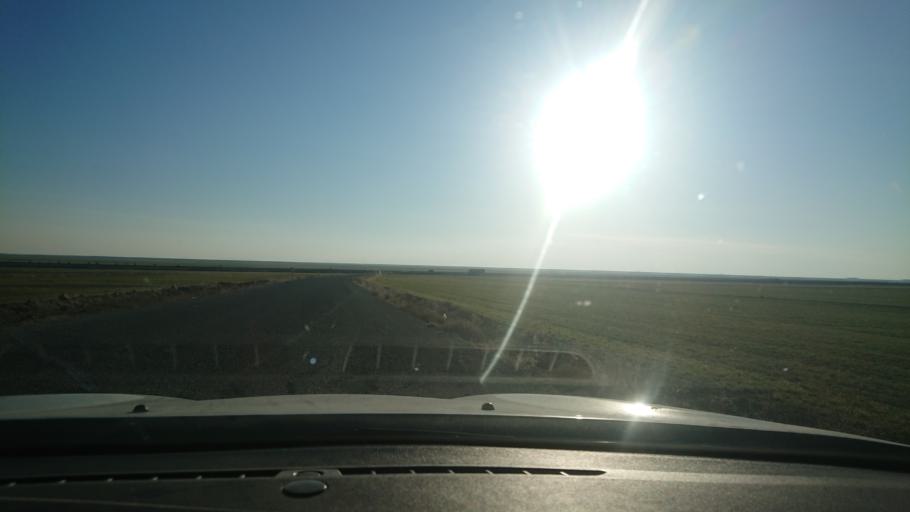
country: TR
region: Aksaray
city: Acipinar
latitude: 38.6658
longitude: 33.7205
